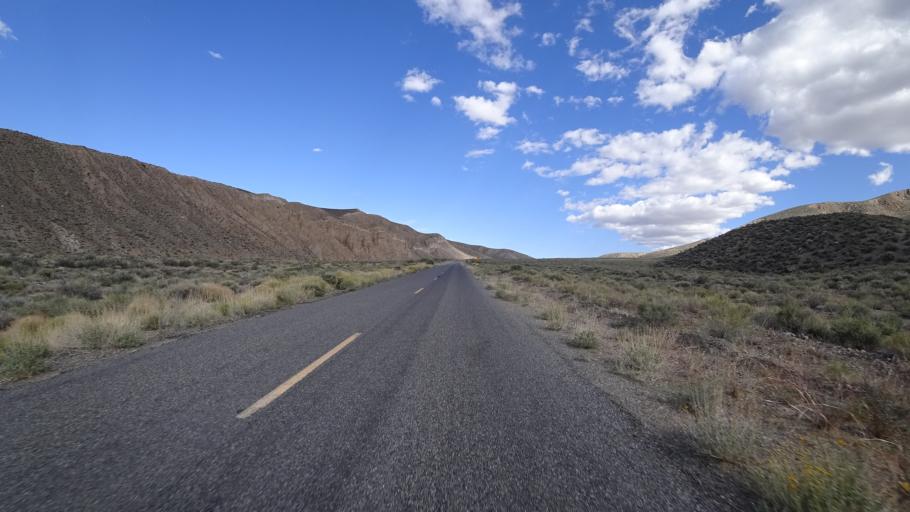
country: US
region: Nevada
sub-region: Nye County
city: Beatty
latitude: 36.4097
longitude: -117.1747
